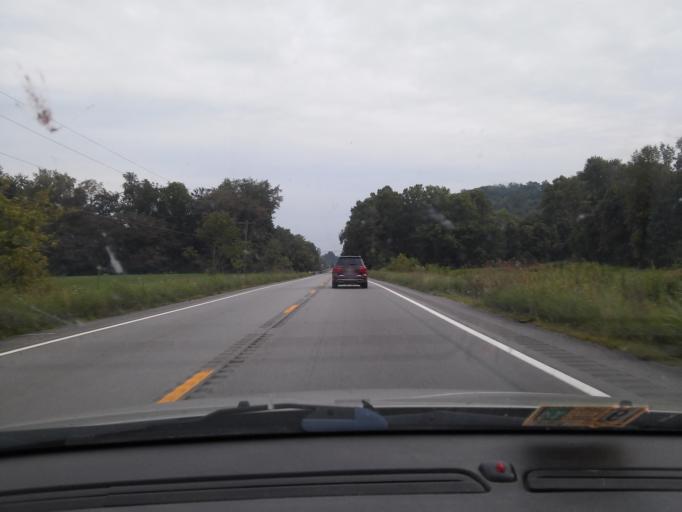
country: US
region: West Virginia
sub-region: Putnam County
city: Buffalo
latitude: 38.6262
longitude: -81.9830
